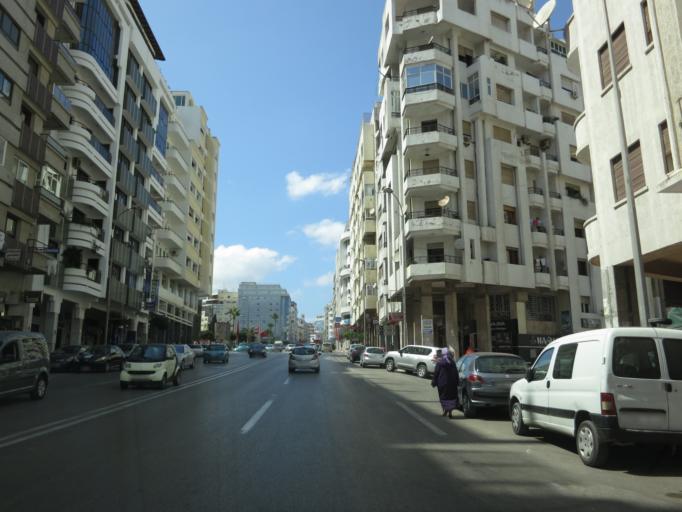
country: MA
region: Tanger-Tetouan
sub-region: Tanger-Assilah
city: Tangier
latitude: 35.7758
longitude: -5.8013
